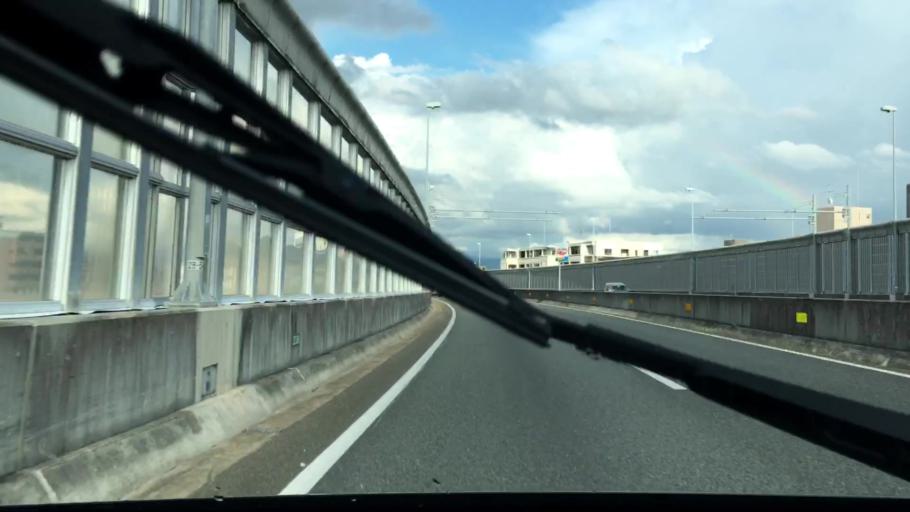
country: JP
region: Fukuoka
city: Fukuoka-shi
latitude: 33.5785
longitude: 130.3244
